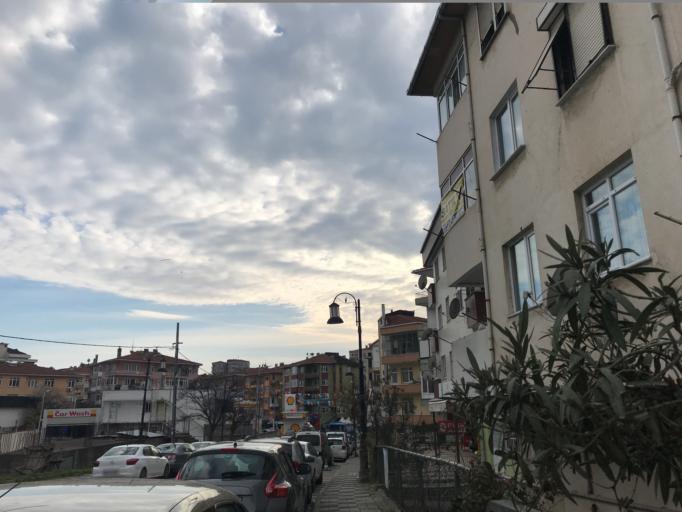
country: TR
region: Istanbul
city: Maltepe
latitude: 40.9302
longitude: 29.1298
